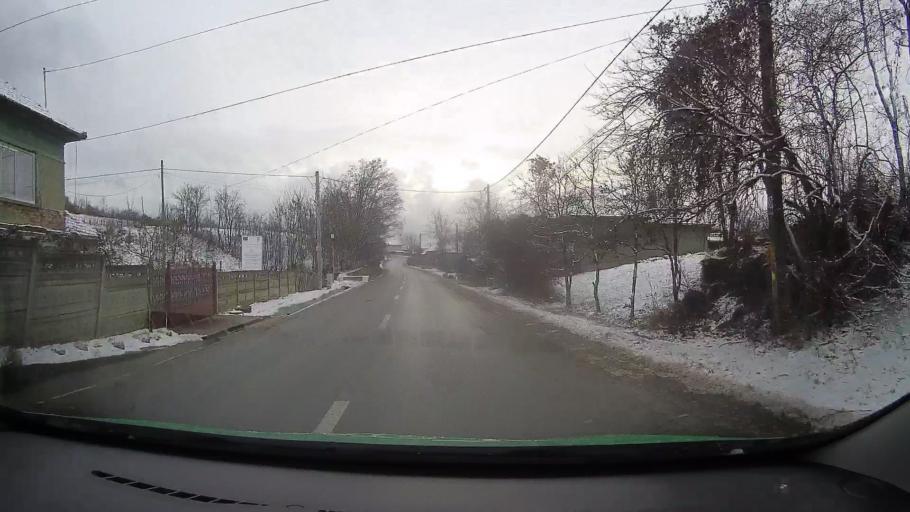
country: RO
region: Hunedoara
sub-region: Oras Hateg
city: Hateg
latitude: 45.6236
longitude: 22.9371
